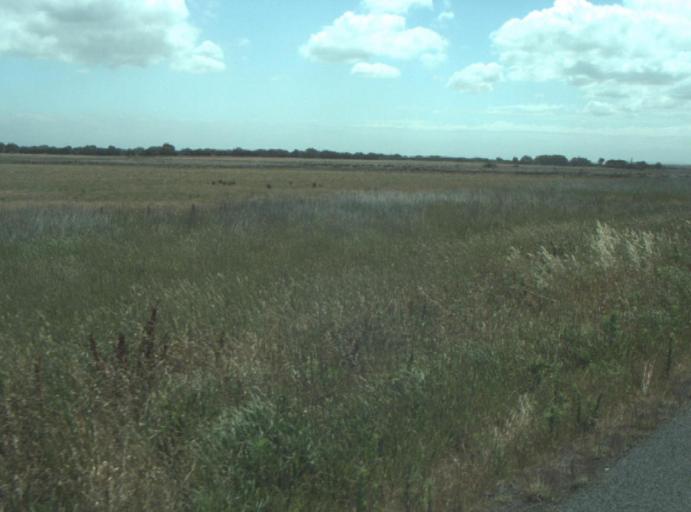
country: AU
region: Victoria
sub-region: Greater Geelong
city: Breakwater
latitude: -38.2887
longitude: 144.3935
